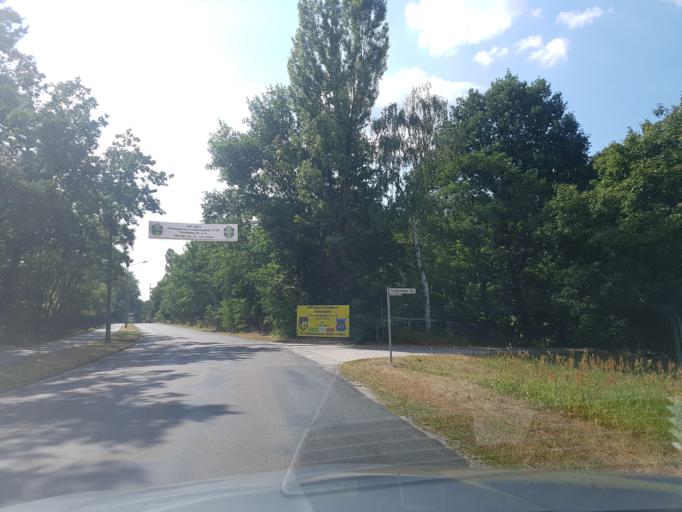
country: DE
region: Brandenburg
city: Doberlug-Kirchhain
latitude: 51.6285
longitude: 13.5713
